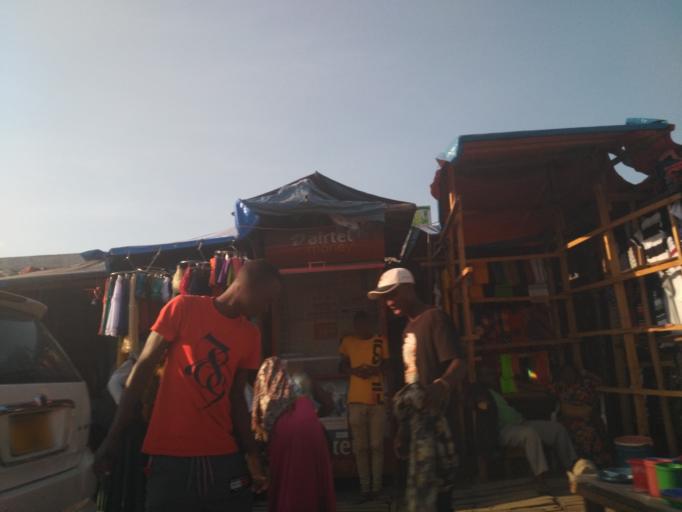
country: TZ
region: Pwani
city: Vikindu
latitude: -6.9194
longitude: 39.2697
